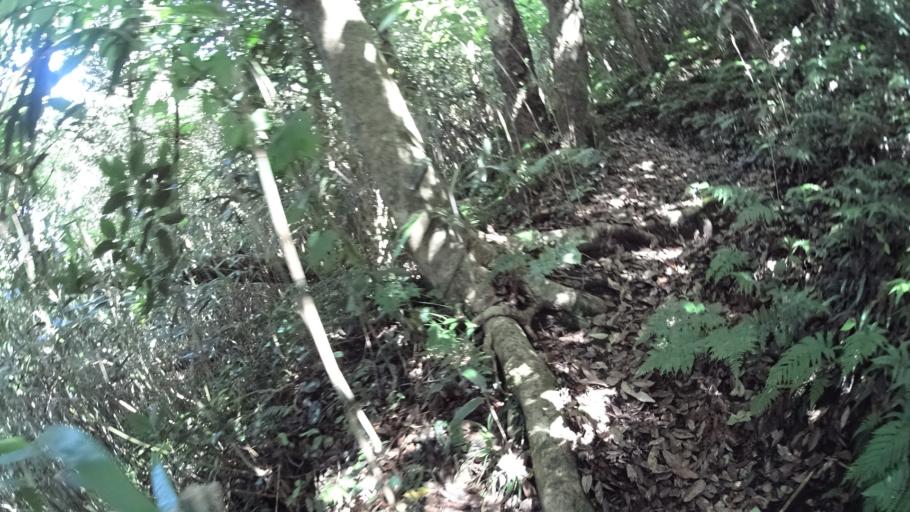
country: JP
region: Shizuoka
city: Shimoda
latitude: 34.5170
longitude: 139.2774
